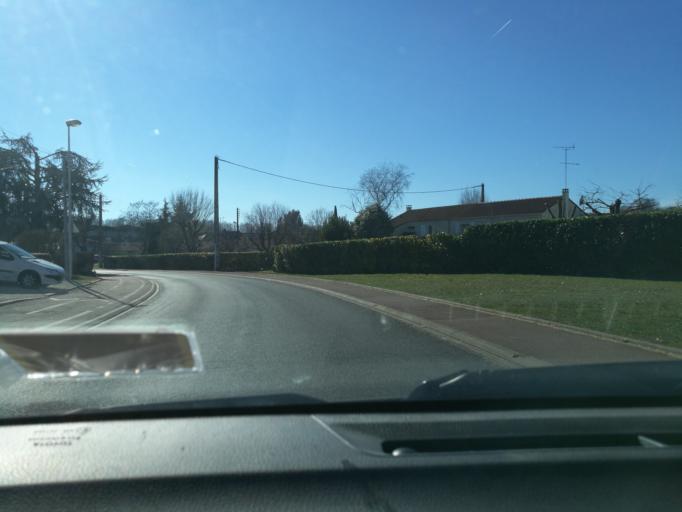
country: FR
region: Centre
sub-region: Departement du Loiret
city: Saint-Jean-de-la-Ruelle
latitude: 47.8986
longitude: 1.8651
